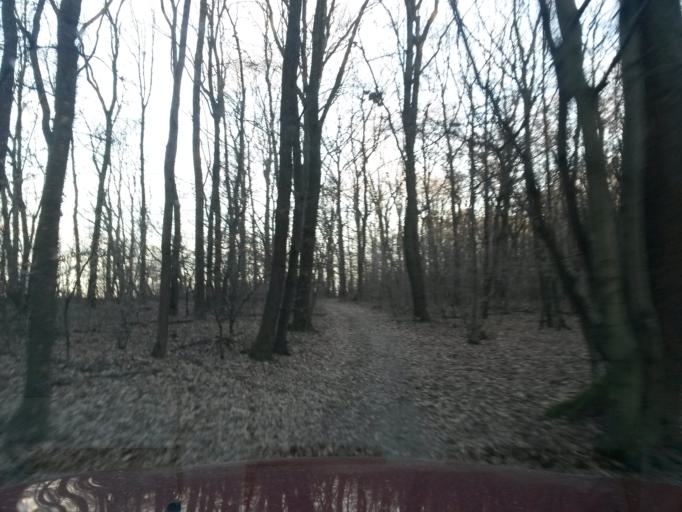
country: SK
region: Kosicky
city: Kosice
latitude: 48.7054
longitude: 21.3022
